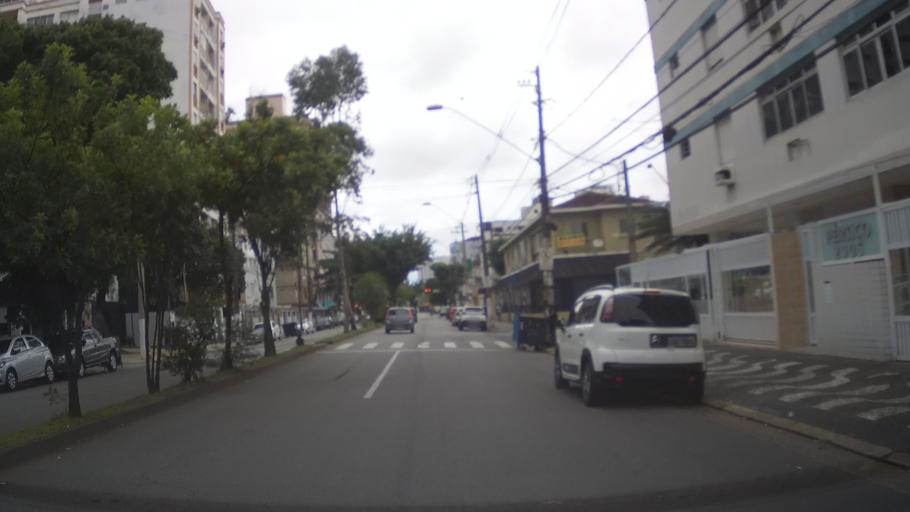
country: BR
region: Sao Paulo
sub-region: Santos
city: Santos
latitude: -23.9645
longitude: -46.3170
